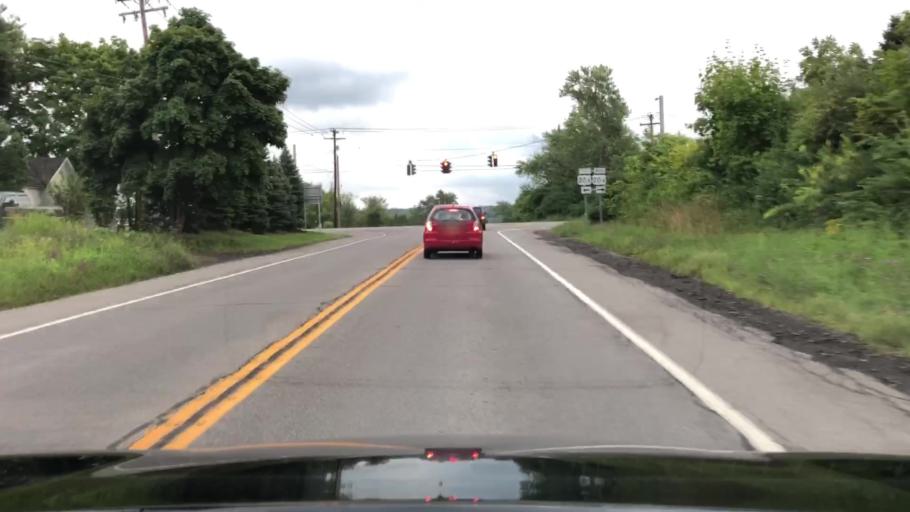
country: US
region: New York
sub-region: Erie County
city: Orchard Park
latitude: 42.7694
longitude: -78.6969
